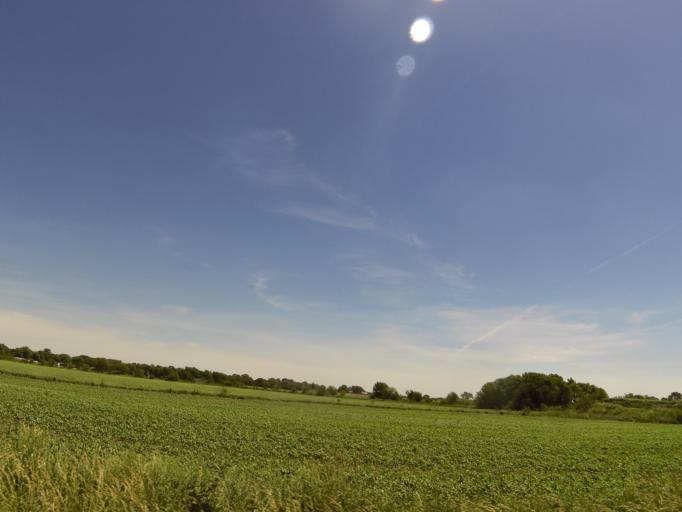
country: US
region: Illinois
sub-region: Vermilion County
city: Hoopeston
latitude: 40.4545
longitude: -87.6870
